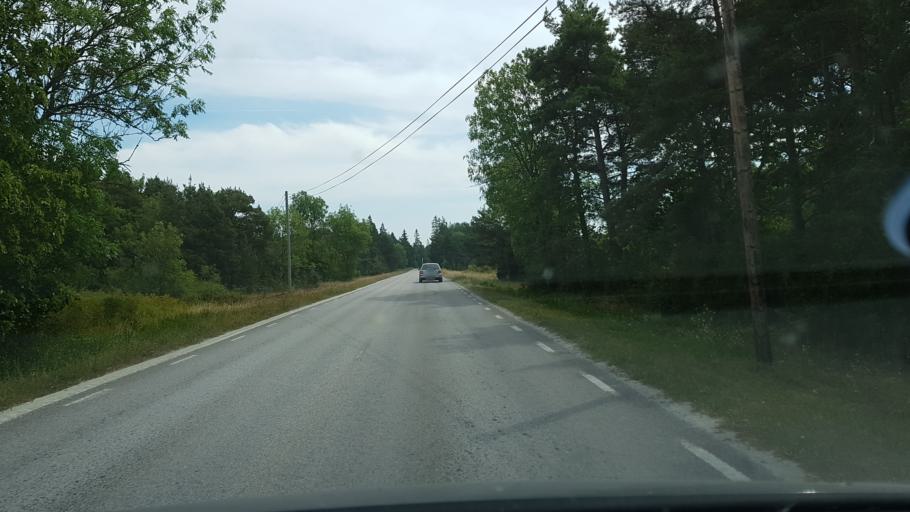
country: SE
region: Gotland
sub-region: Gotland
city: Slite
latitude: 57.7454
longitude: 18.7357
